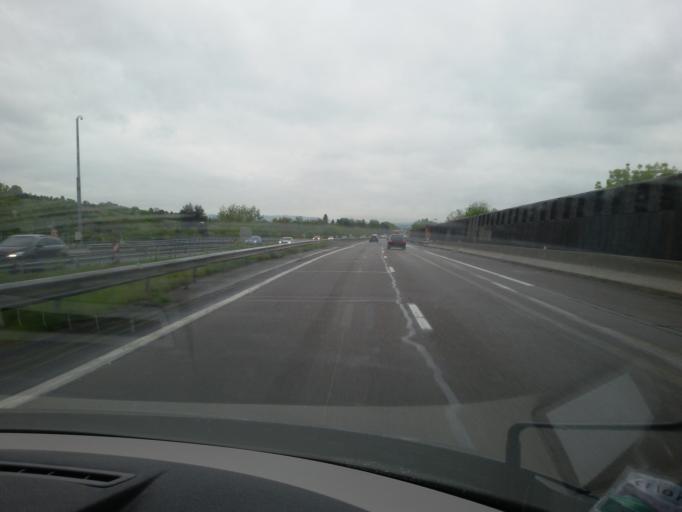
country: FR
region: Rhone-Alpes
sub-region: Departement du Rhone
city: Lissieu
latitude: 45.8593
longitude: 4.7417
